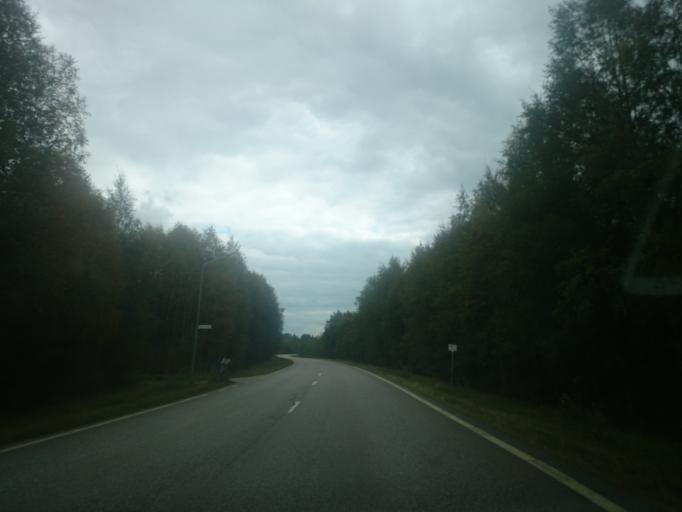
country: SE
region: Jaemtland
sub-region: Harjedalens Kommun
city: Sveg
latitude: 62.1302
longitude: 14.0592
